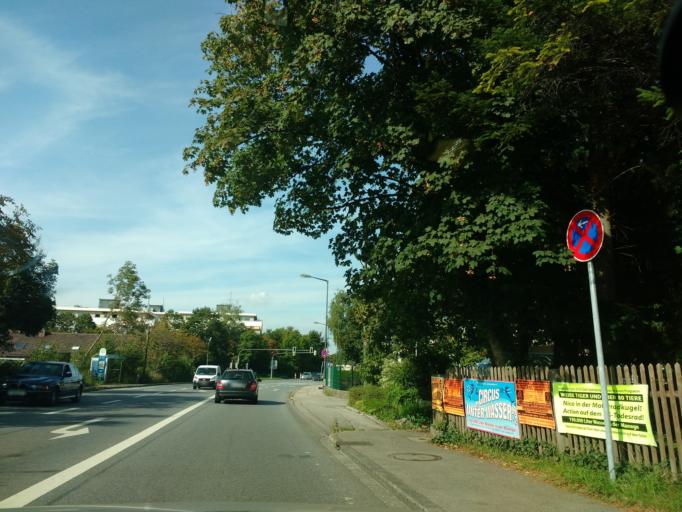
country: DE
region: Bavaria
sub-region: Upper Bavaria
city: Grafelfing
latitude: 48.1244
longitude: 11.4473
